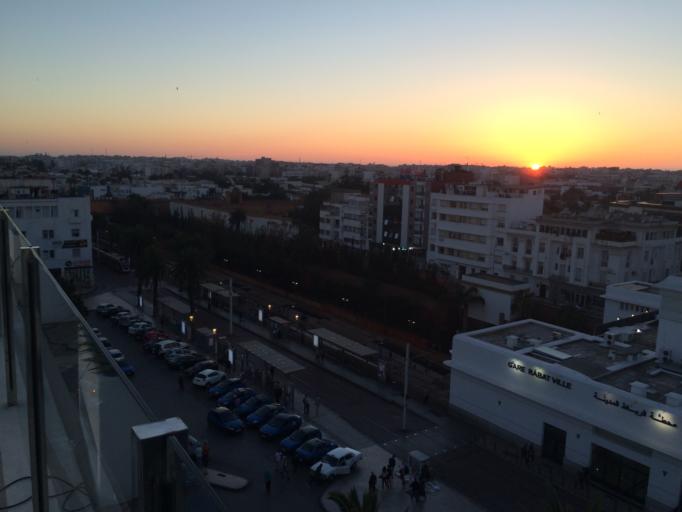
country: MA
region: Rabat-Sale-Zemmour-Zaer
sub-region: Rabat
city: Rabat
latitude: 34.0160
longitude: -6.8353
